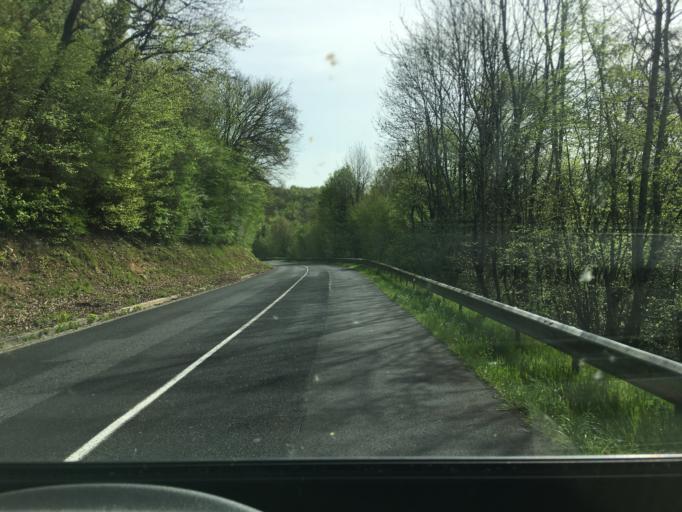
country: FR
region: Lorraine
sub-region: Departement de Meurthe-et-Moselle
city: Velaine-en-Haye
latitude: 48.6638
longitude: 6.0184
